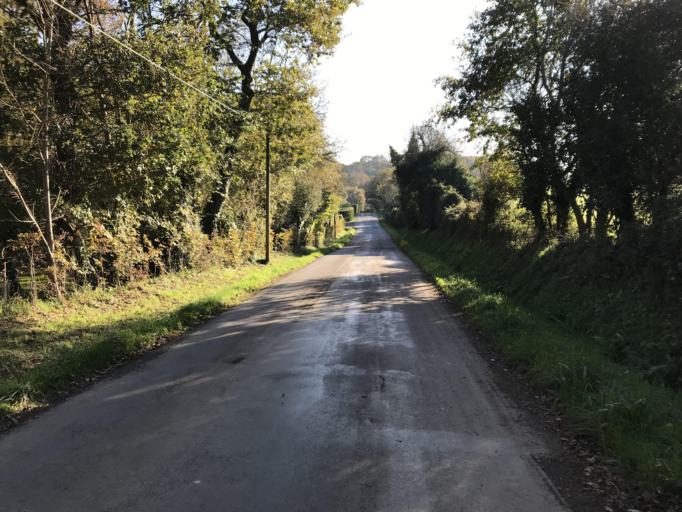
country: FR
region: Brittany
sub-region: Departement du Finistere
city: Hopital-Camfrout
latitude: 48.3215
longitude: -4.2340
